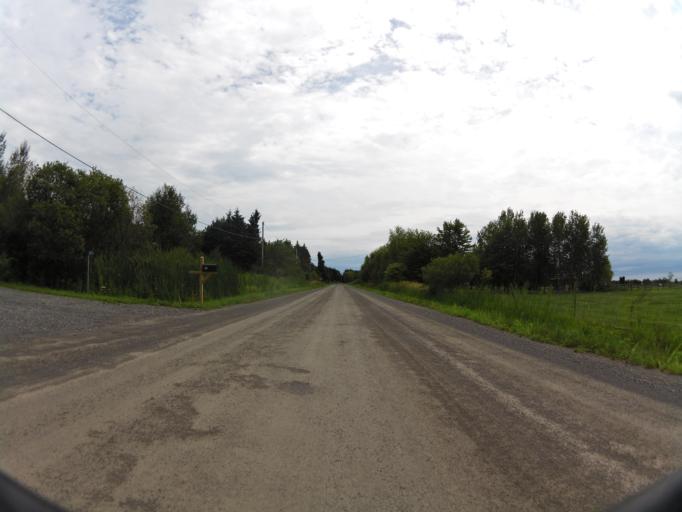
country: CA
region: Ontario
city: Bells Corners
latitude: 45.0746
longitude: -75.6046
